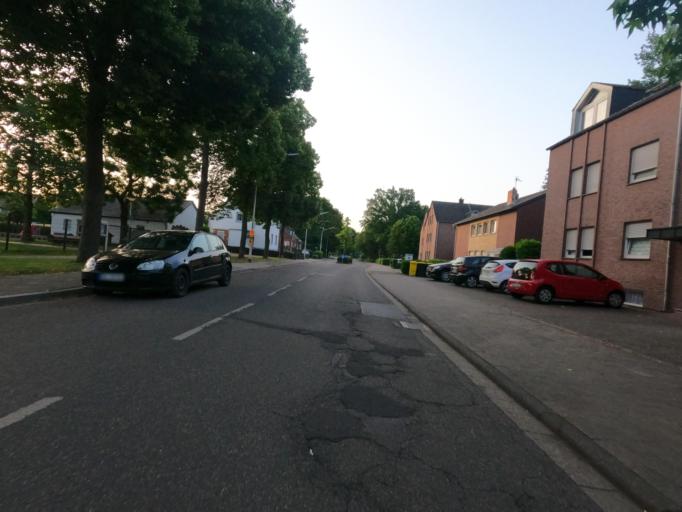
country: DE
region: North Rhine-Westphalia
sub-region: Regierungsbezirk Koln
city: Wassenberg
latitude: 51.0585
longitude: 6.1446
